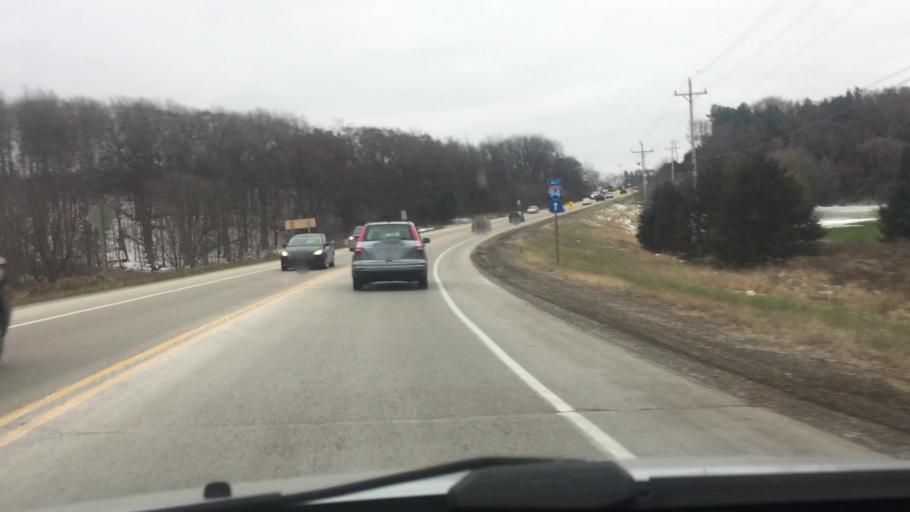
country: US
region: Wisconsin
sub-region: Waukesha County
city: Hartland
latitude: 43.0750
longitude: -88.3636
